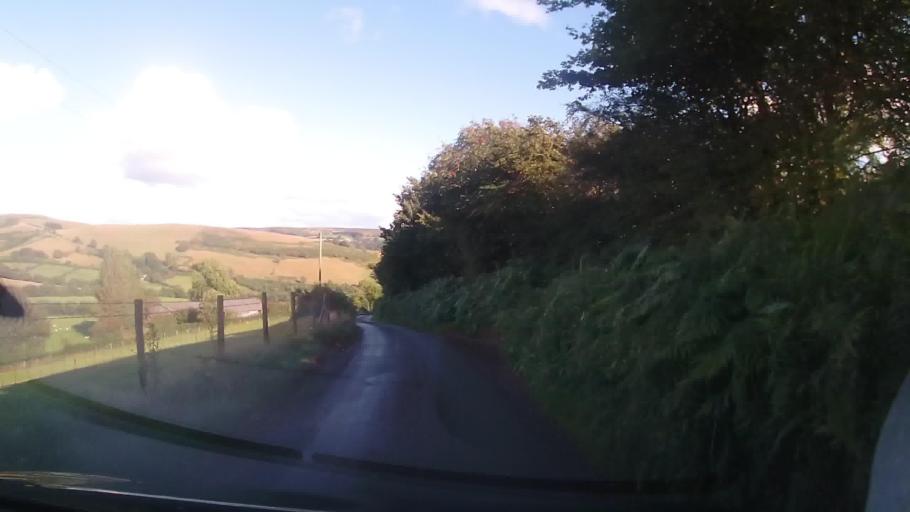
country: GB
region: England
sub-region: Shropshire
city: Norbury
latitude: 52.5682
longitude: -2.9053
